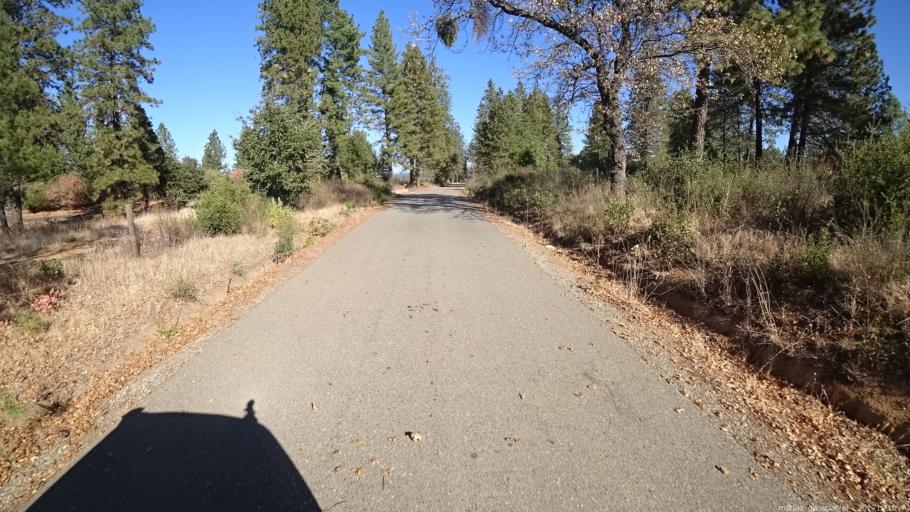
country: US
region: California
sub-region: Shasta County
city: Shingletown
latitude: 40.4636
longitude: -122.0010
